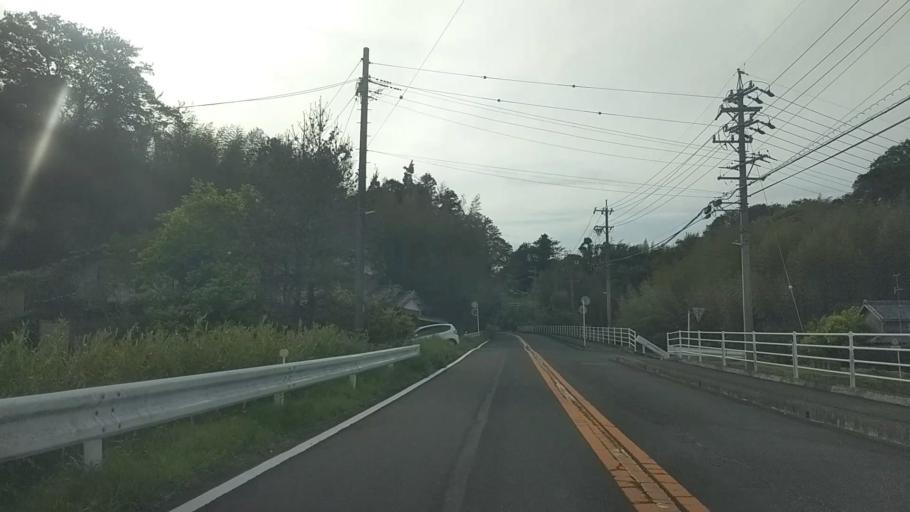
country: JP
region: Shizuoka
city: Kosai-shi
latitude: 34.7462
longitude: 137.6122
